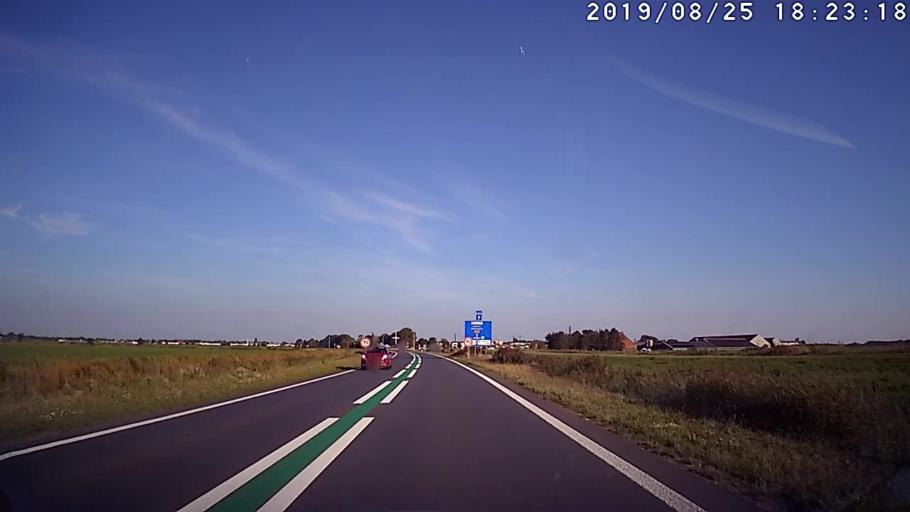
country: NL
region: Friesland
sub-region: Gemeente Lemsterland
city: Lemmer
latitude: 52.8575
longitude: 5.6621
